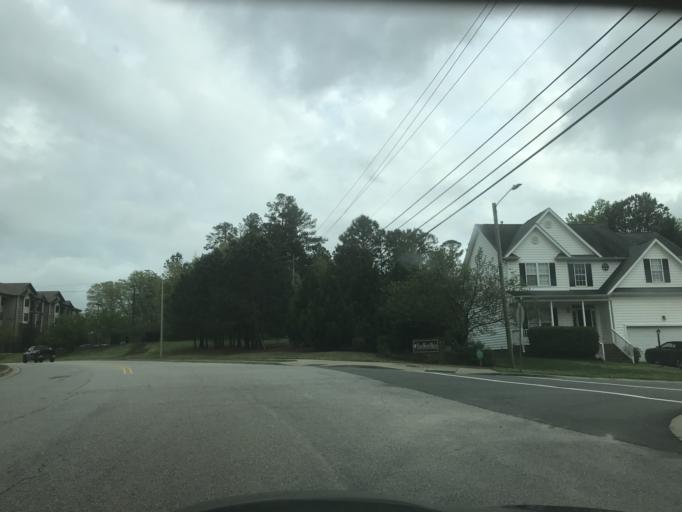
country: US
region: North Carolina
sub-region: Wake County
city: West Raleigh
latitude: 35.7489
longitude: -78.6786
